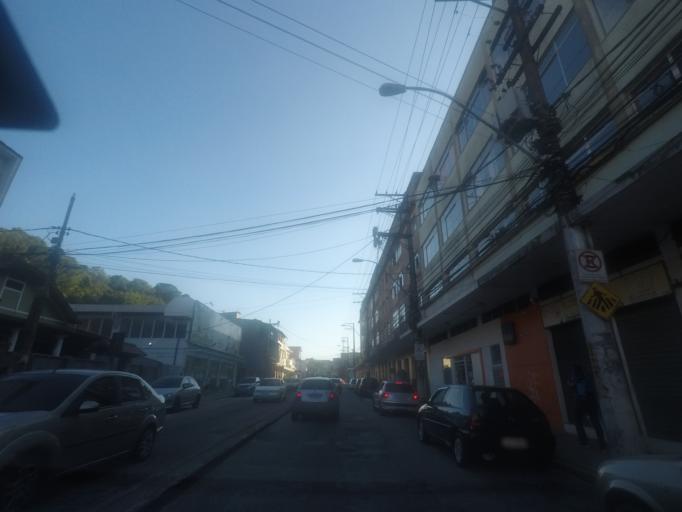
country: BR
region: Rio de Janeiro
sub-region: Petropolis
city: Petropolis
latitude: -22.5251
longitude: -43.1714
